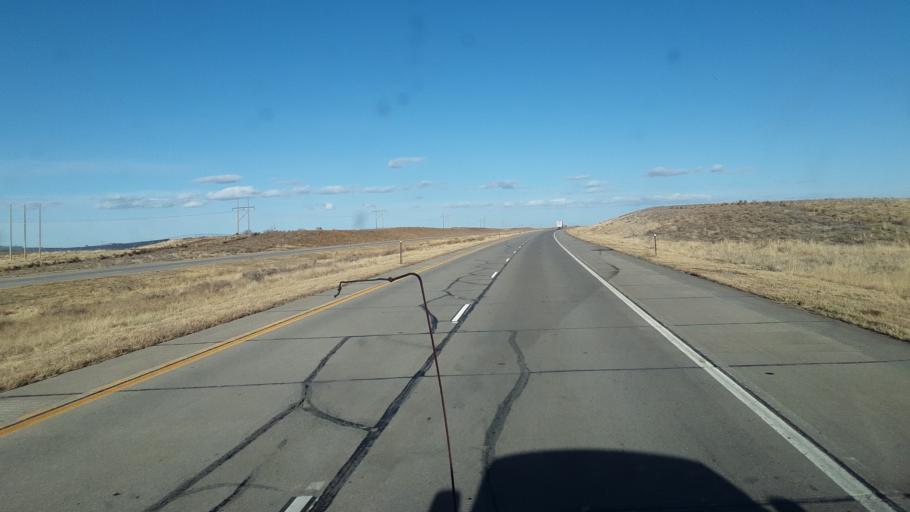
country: US
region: Colorado
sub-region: Logan County
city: Sterling
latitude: 40.6629
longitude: -103.1326
